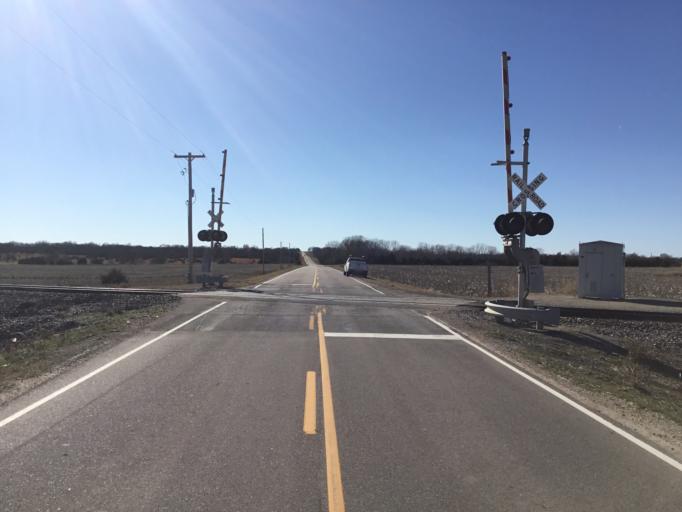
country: US
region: Kansas
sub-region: Sedgwick County
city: Kechi
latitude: 37.8694
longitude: -97.2216
